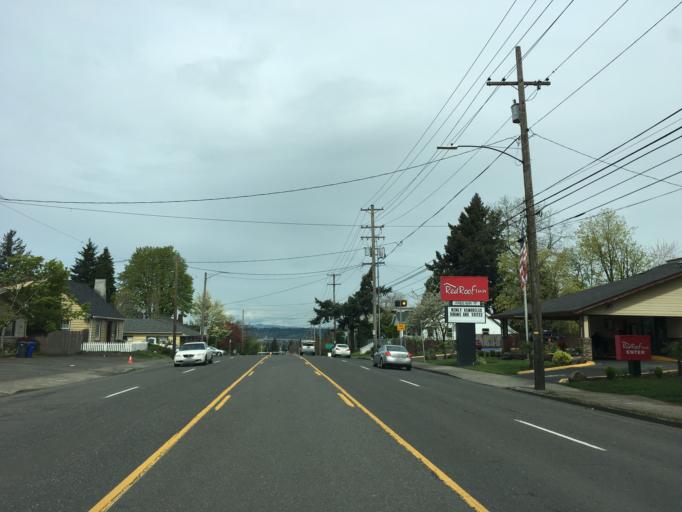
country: US
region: Oregon
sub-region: Multnomah County
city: Lents
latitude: 45.5501
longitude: -122.5787
